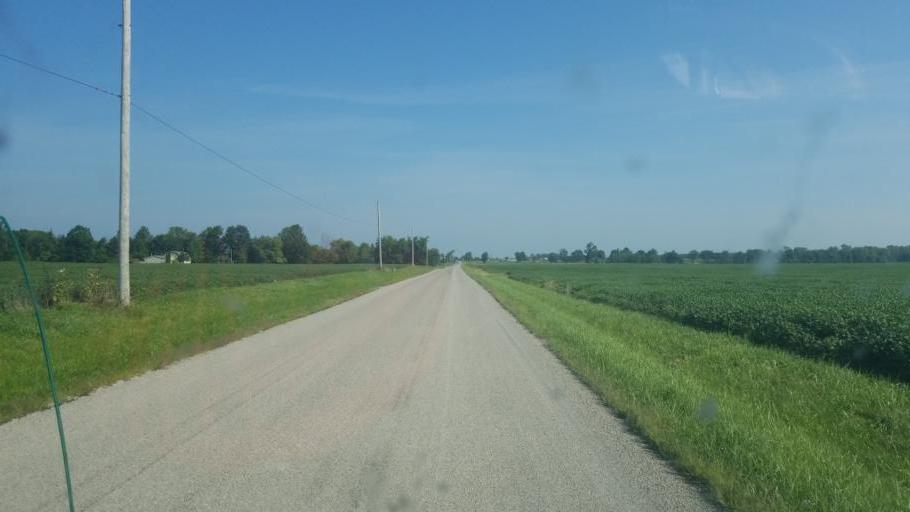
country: US
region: Ohio
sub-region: Lorain County
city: Wellington
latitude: 41.0907
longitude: -82.1810
